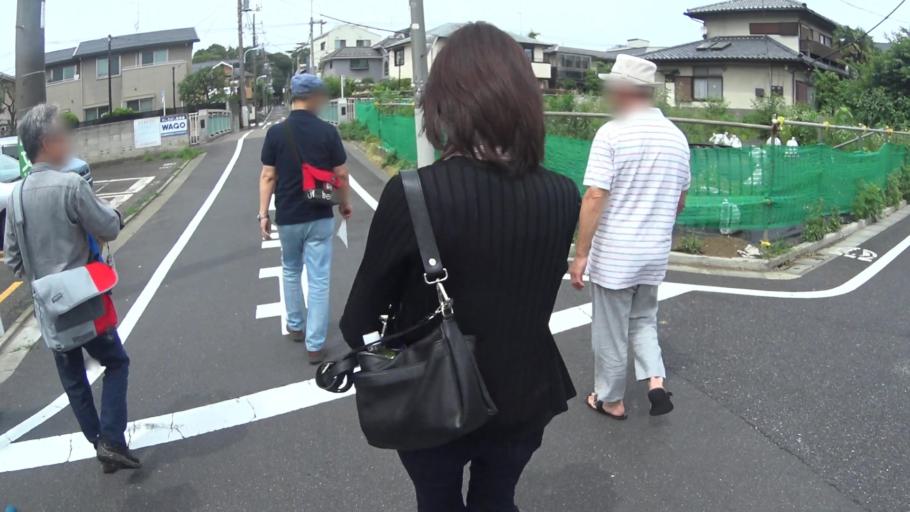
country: JP
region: Tokyo
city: Musashino
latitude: 35.7083
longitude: 139.6058
